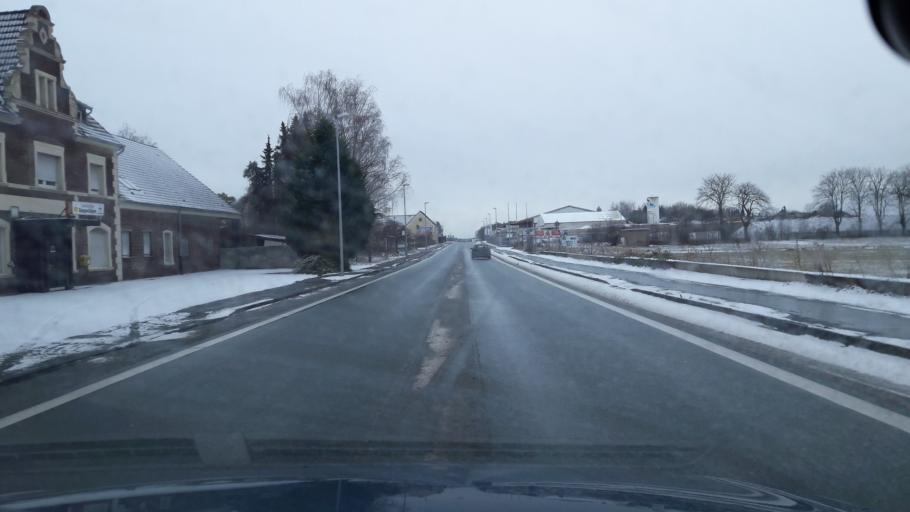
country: DE
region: North Rhine-Westphalia
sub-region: Regierungsbezirk Munster
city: Ennigerloh
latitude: 51.8208
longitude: 8.0254
